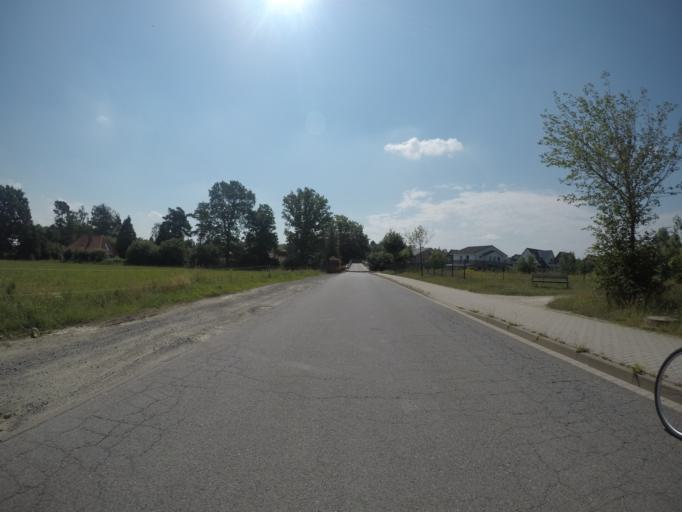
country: DE
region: Lower Saxony
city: Buchholz in der Nordheide
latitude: 53.3372
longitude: 9.8497
